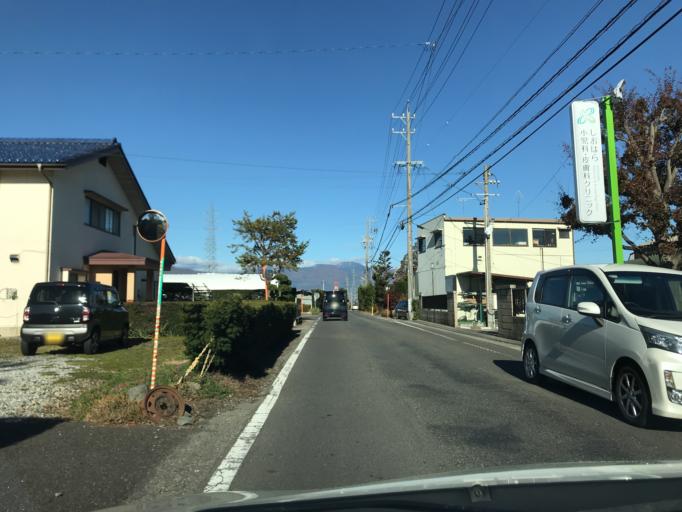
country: JP
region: Nagano
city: Shiojiri
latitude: 36.1204
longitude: 137.9431
